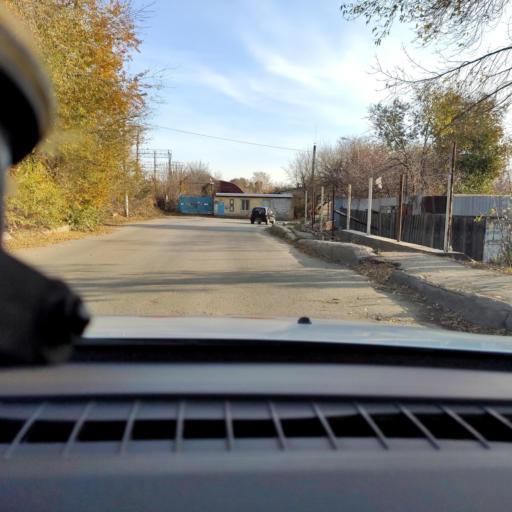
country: RU
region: Samara
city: Samara
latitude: 53.1781
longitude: 50.1468
